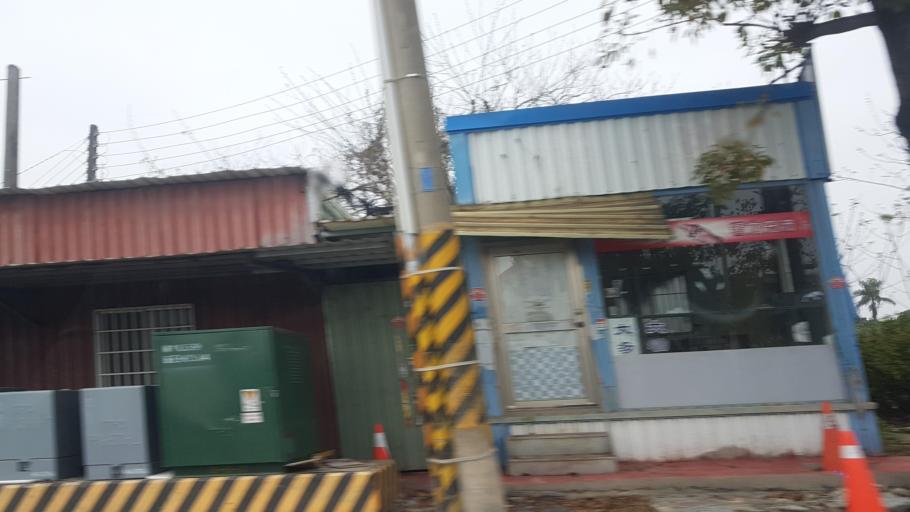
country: TW
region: Taiwan
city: Xinying
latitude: 23.3186
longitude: 120.3061
